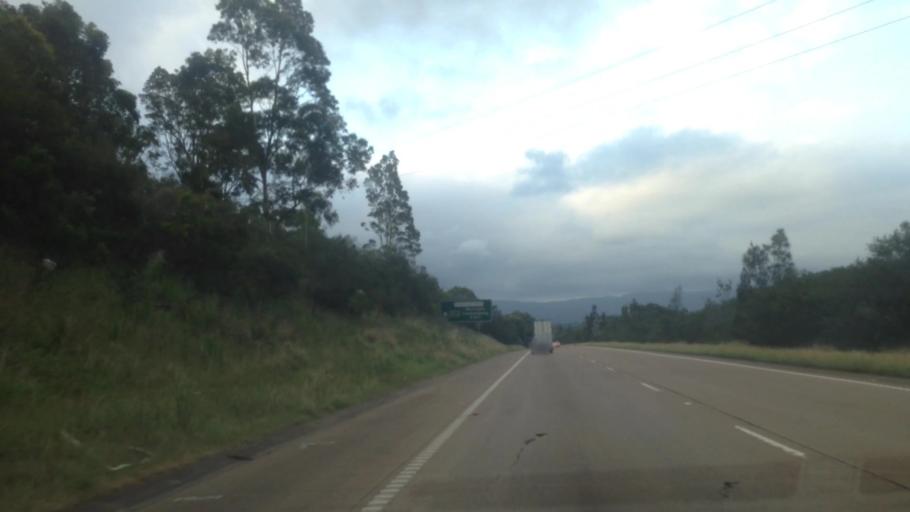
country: AU
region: New South Wales
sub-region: Lake Macquarie Shire
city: Cooranbong
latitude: -33.1258
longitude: 151.4695
